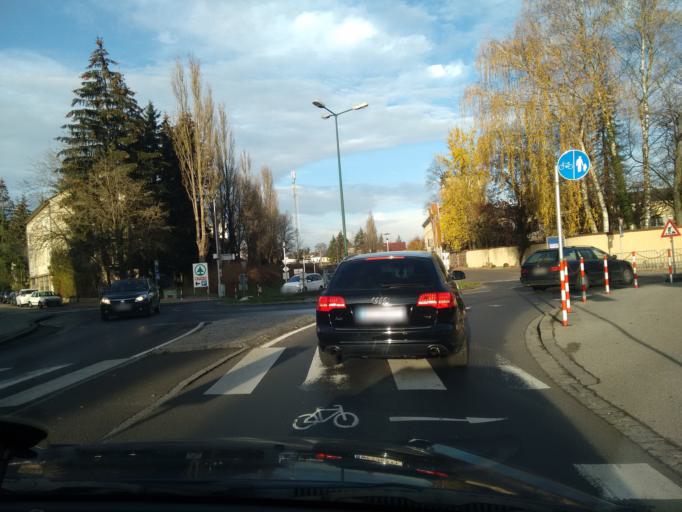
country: AT
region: Upper Austria
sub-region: Wels Stadt
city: Wels
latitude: 48.1615
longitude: 14.0176
